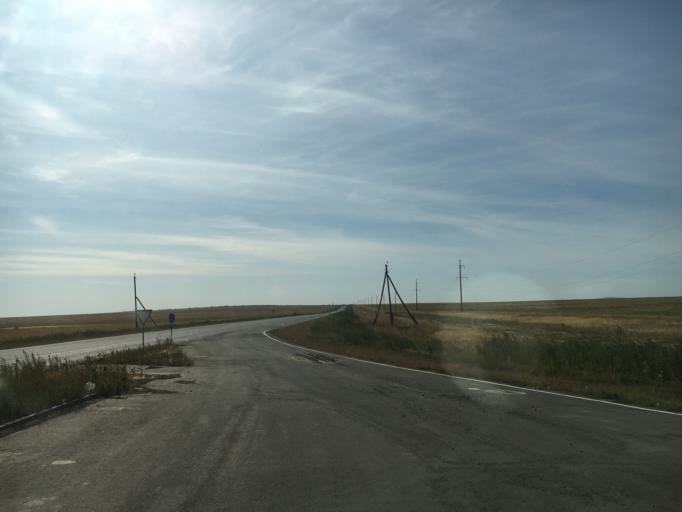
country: KZ
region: Batys Qazaqstan
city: Peremetnoe
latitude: 51.1172
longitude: 50.6227
